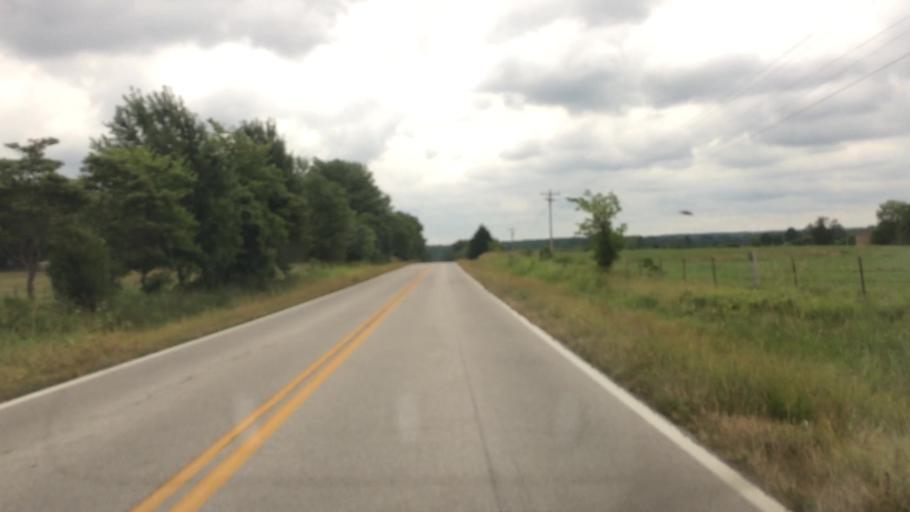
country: US
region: Missouri
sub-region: Greene County
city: Strafford
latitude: 37.2855
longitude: -93.1013
